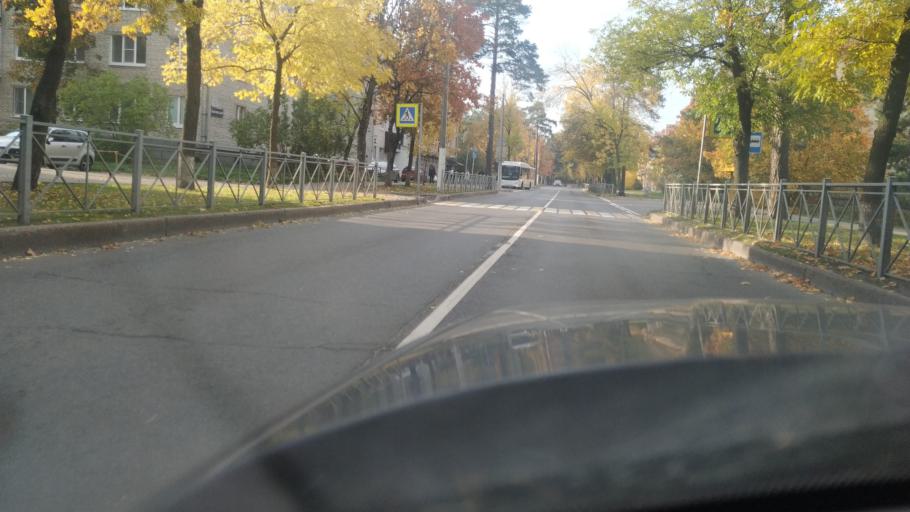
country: RU
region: Leningrad
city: Sosnovyy Bor
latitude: 59.8896
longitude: 29.0908
